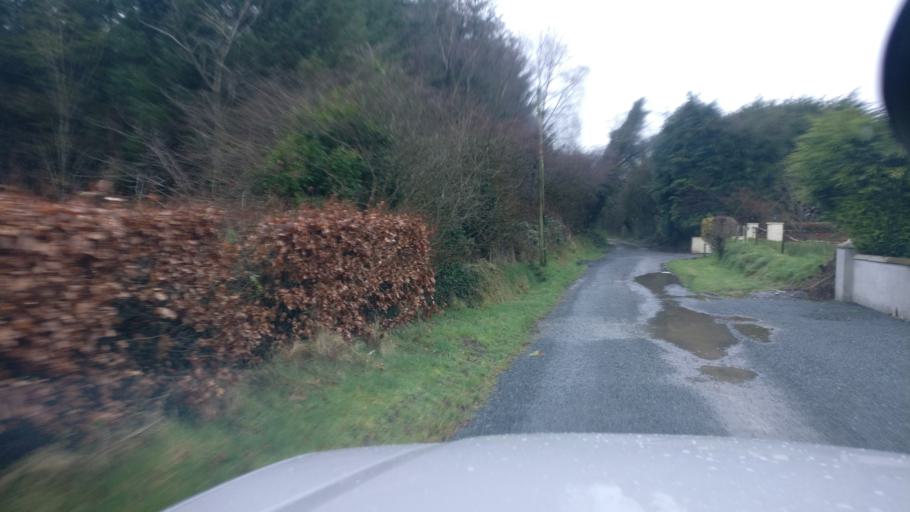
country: IE
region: Connaught
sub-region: County Galway
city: Ballinasloe
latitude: 53.2529
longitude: -8.3638
